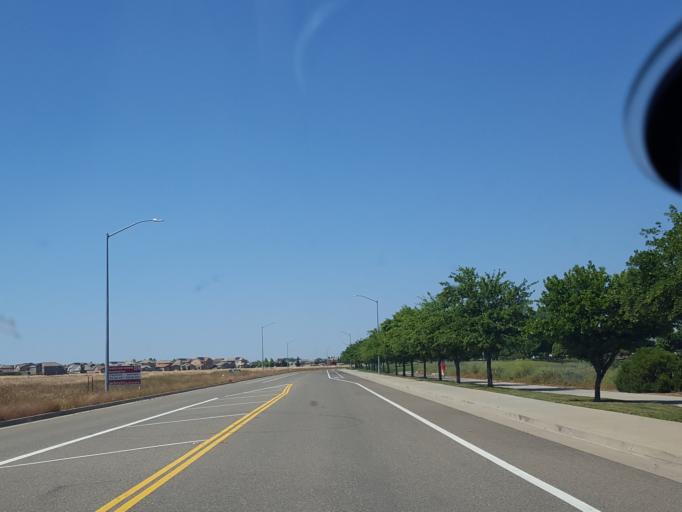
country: US
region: California
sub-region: Sacramento County
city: Rancho Cordova
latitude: 38.5694
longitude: -121.2795
